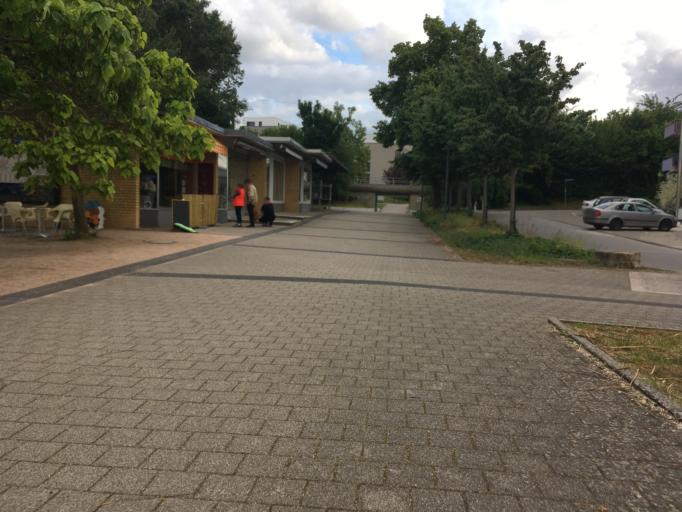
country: DE
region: Baden-Wuerttemberg
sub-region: Regierungsbezirk Stuttgart
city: Bad Rappenau
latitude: 49.2395
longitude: 9.1080
